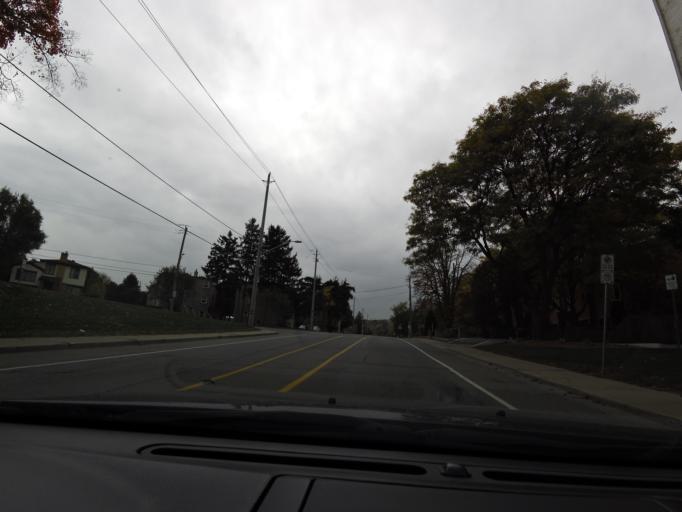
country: CA
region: Ontario
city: Ancaster
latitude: 43.2556
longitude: -79.9368
